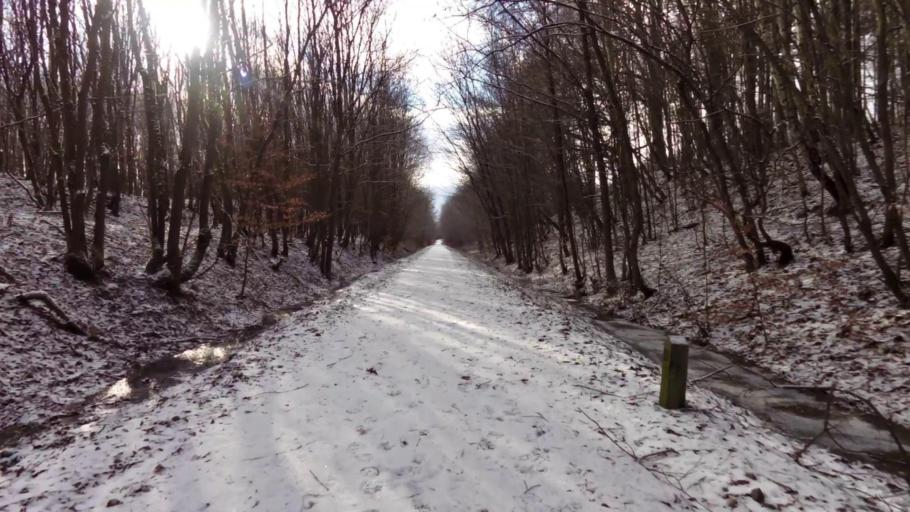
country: PL
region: West Pomeranian Voivodeship
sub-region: Powiat swidwinski
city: Polczyn-Zdroj
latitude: 53.7418
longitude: 16.0550
